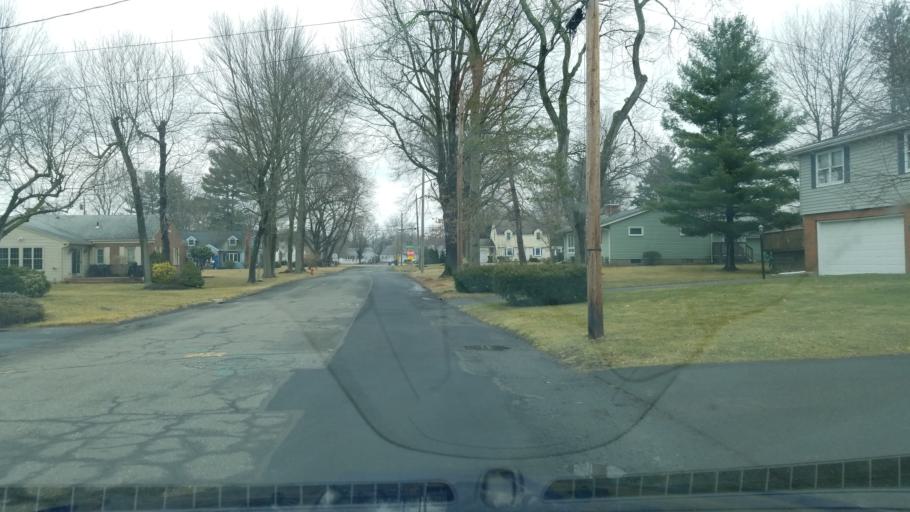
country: US
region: Connecticut
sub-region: Hartford County
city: Wethersfield
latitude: 41.6943
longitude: -72.6720
